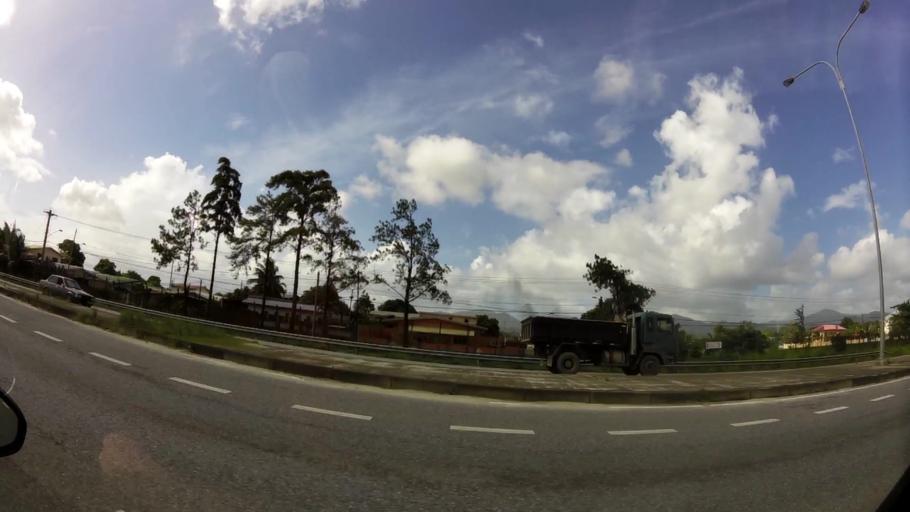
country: TT
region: Borough of Arima
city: Arima
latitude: 10.6159
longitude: -61.2592
